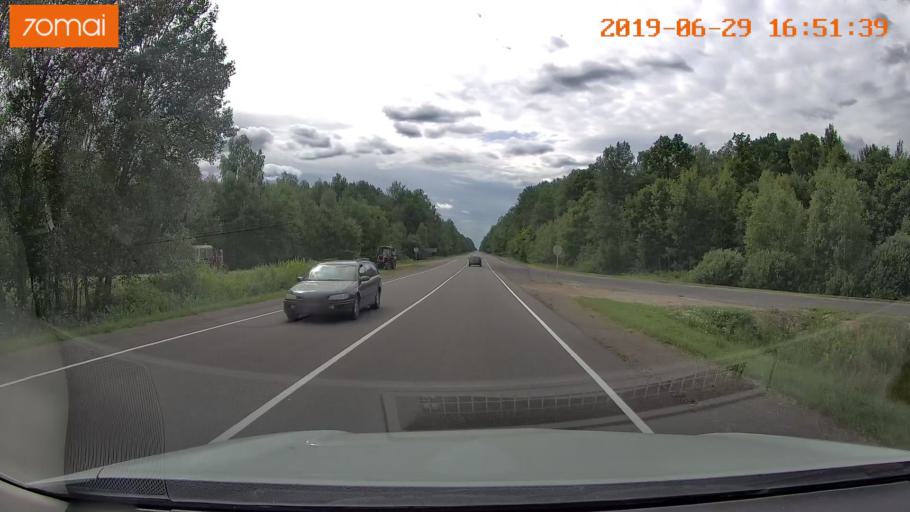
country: BY
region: Brest
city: Horad Luninyets
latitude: 52.2816
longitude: 26.8213
